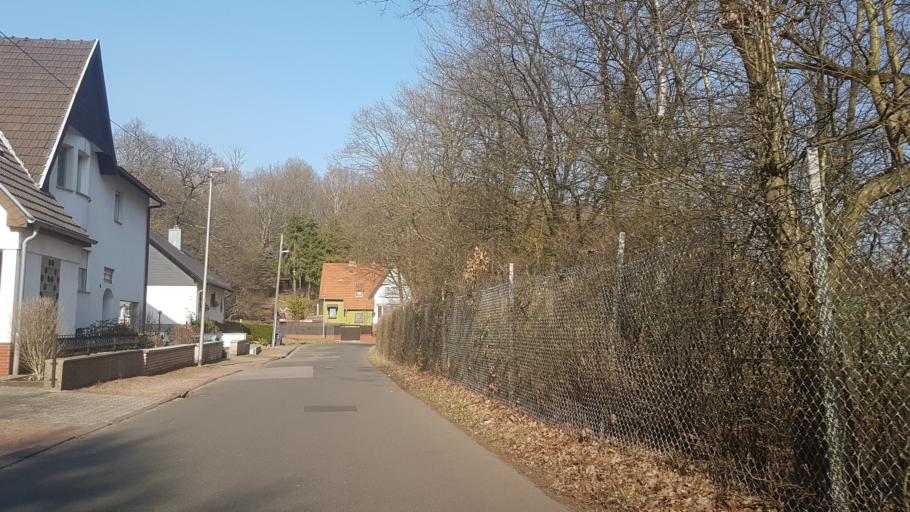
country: DE
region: Saarland
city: Saarbrucken
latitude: 49.2650
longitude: 6.9988
